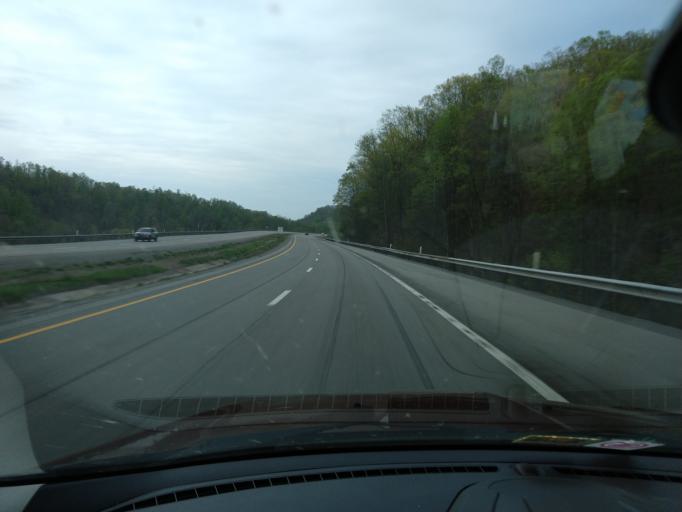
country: US
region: West Virginia
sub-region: Lewis County
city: Weston
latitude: 38.9180
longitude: -80.5595
